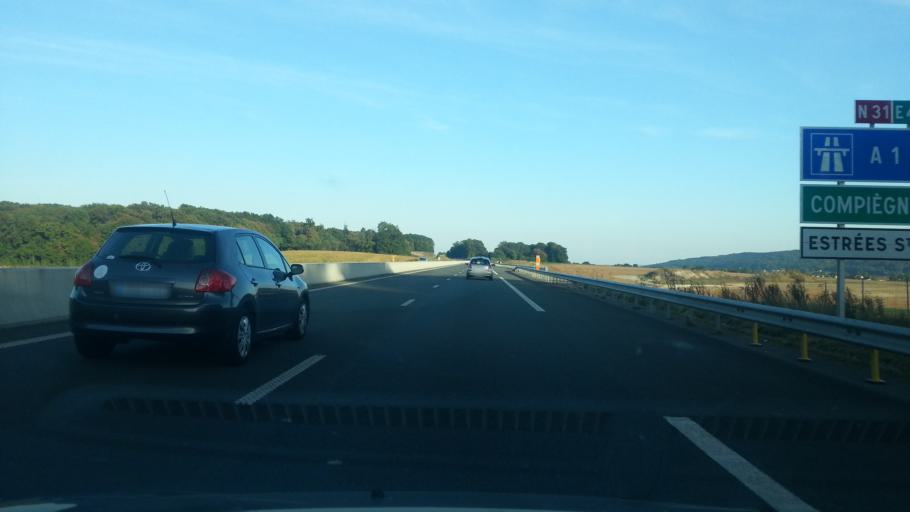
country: FR
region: Picardie
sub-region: Departement de l'Oise
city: Breuil-le-Sec
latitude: 49.3858
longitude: 2.4688
